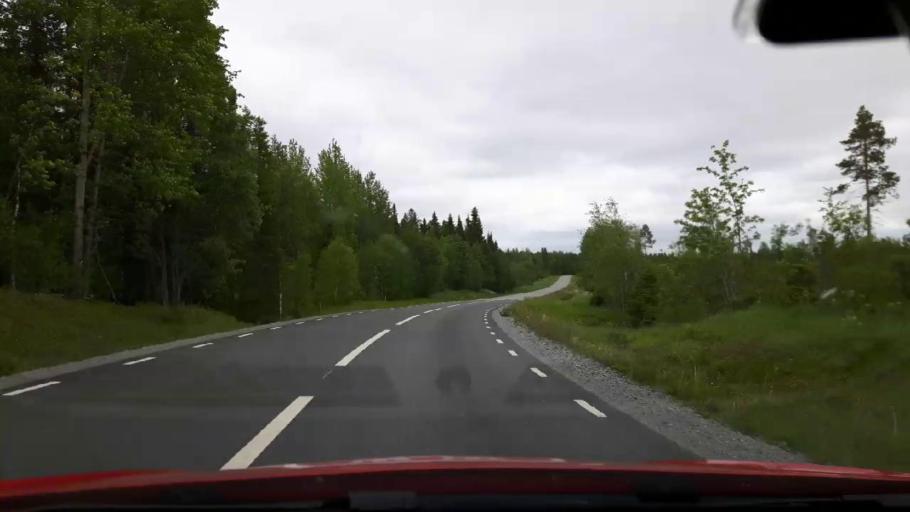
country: SE
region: Jaemtland
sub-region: OEstersunds Kommun
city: Lit
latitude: 63.7359
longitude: 14.8874
